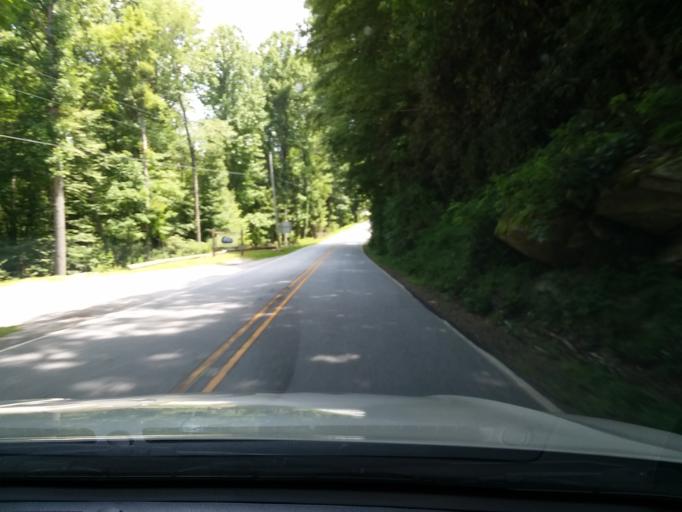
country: US
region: Georgia
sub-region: Rabun County
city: Mountain City
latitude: 35.0051
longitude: -83.3320
